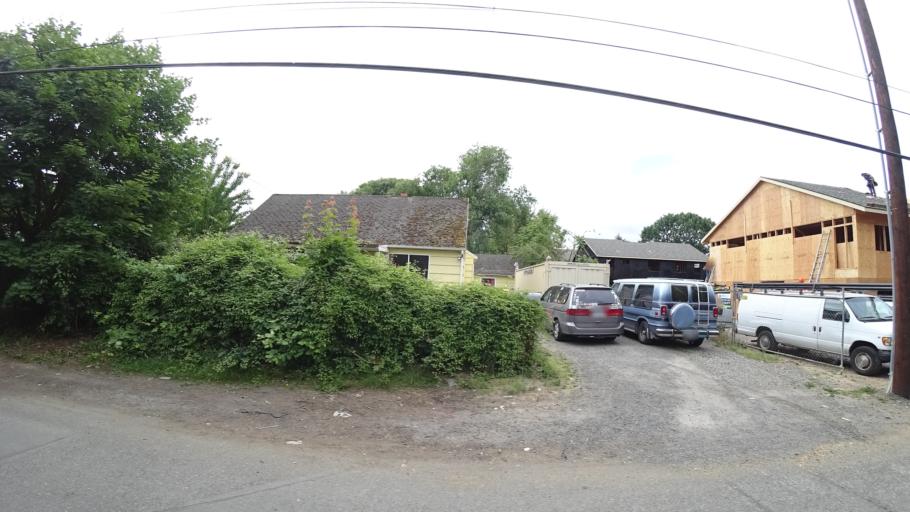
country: US
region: Oregon
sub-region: Multnomah County
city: Lents
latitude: 45.5005
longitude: -122.5757
